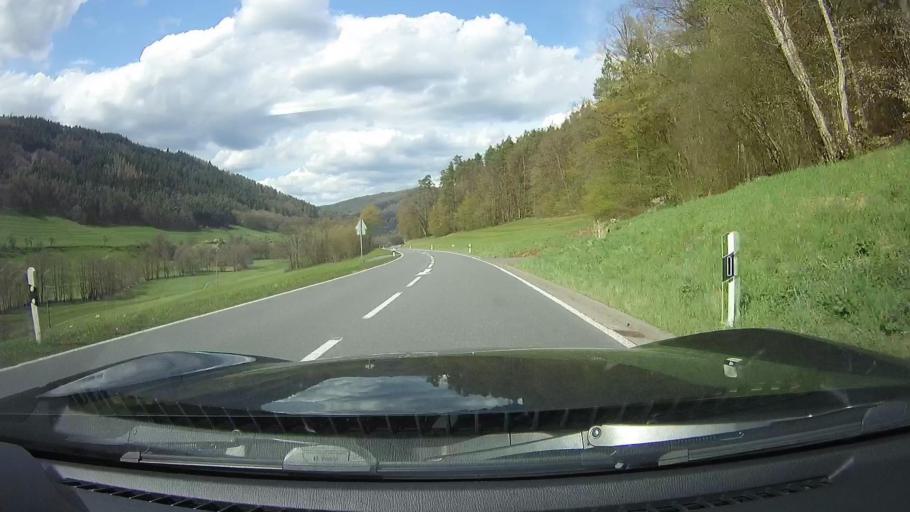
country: DE
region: Bavaria
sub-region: Regierungsbezirk Unterfranken
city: Kirchzell
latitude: 49.6035
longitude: 9.2013
